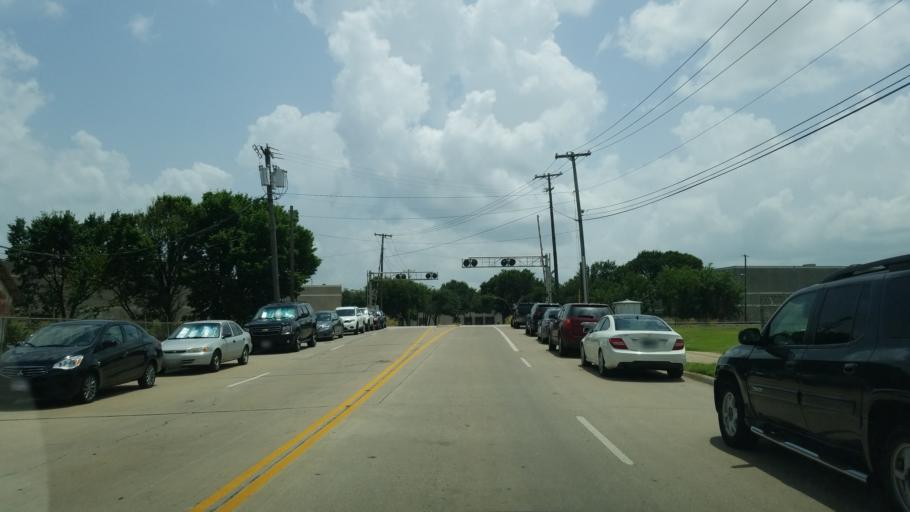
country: US
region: Texas
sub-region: Dallas County
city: Cockrell Hill
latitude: 32.7764
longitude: -96.8825
